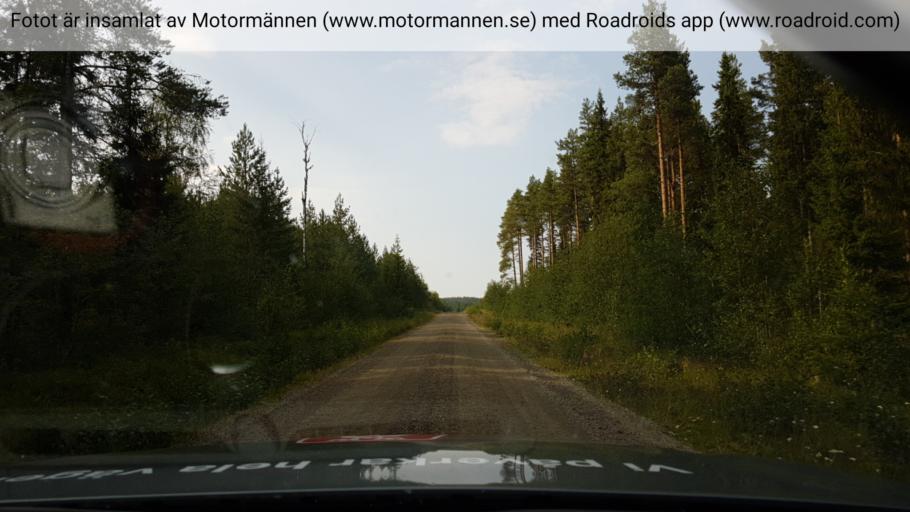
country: SE
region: Jaemtland
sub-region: Bergs Kommun
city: Hoverberg
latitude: 62.5381
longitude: 14.9069
